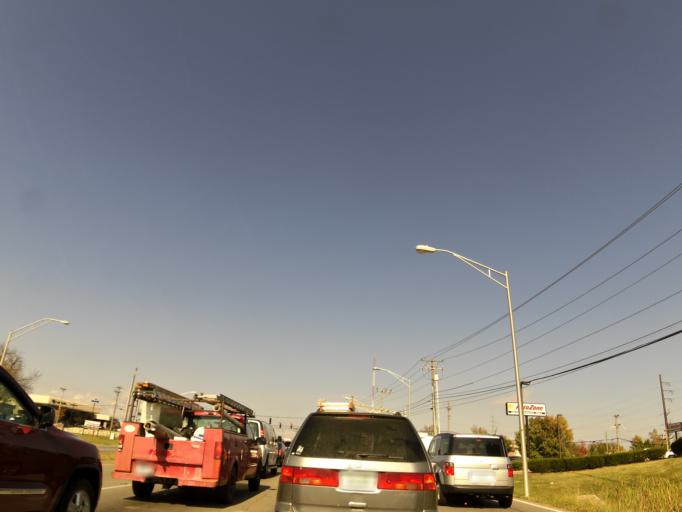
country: US
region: Kentucky
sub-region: Fayette County
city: Lexington-Fayette
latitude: 38.0283
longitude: -84.4526
